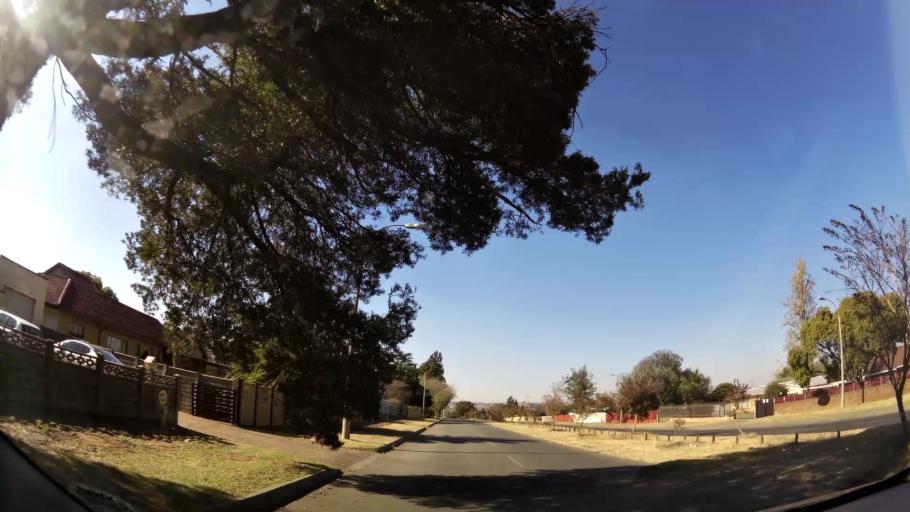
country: ZA
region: Gauteng
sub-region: City of Johannesburg Metropolitan Municipality
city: Roodepoort
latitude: -26.1510
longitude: 27.8292
